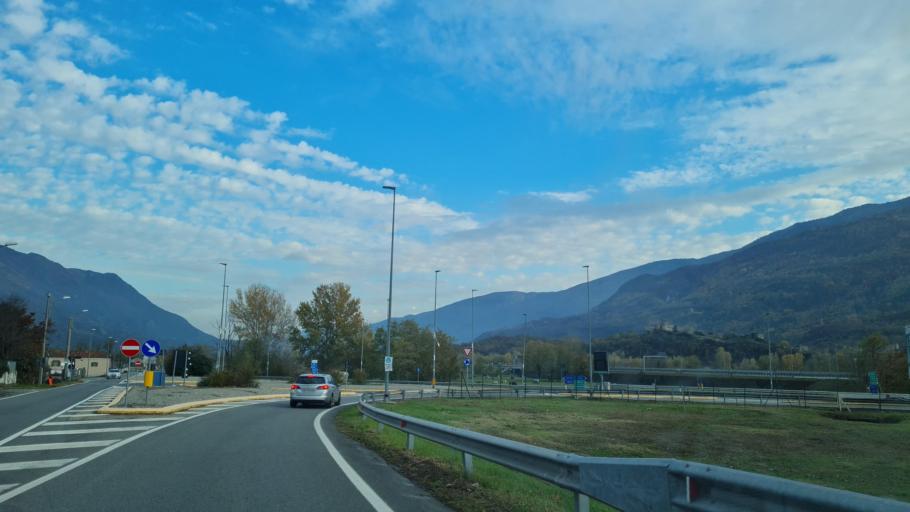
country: IT
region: Piedmont
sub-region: Provincia di Torino
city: San Giorio
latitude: 45.1360
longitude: 7.1741
